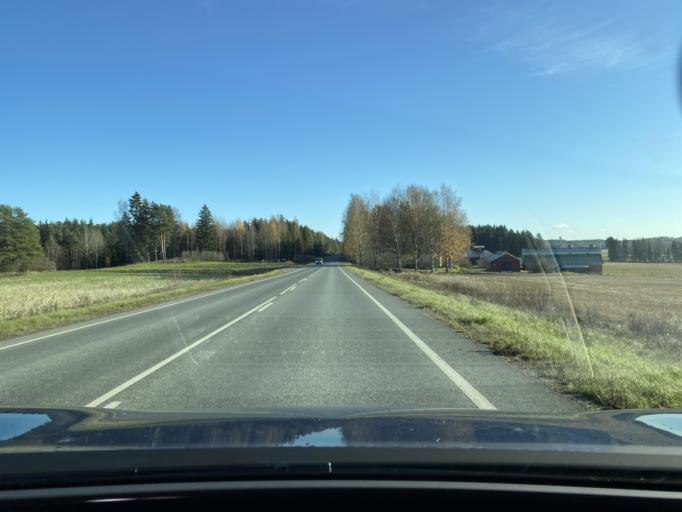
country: FI
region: Haeme
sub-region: Haemeenlinna
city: Parola
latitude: 61.0160
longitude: 24.3574
